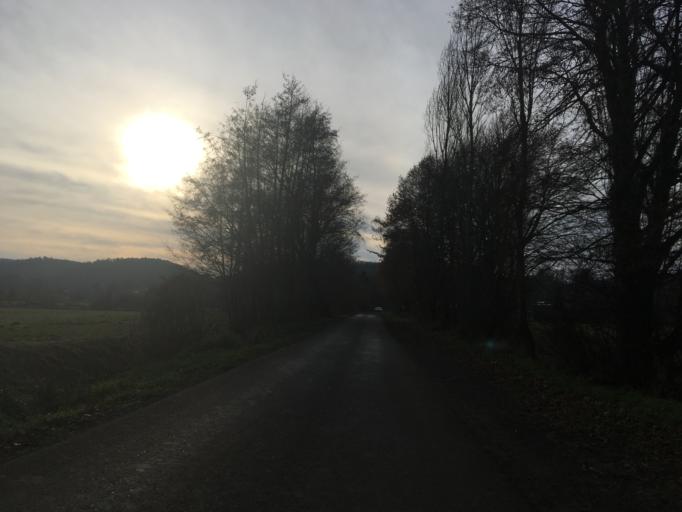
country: DE
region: Brandenburg
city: Falkenberg
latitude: 52.8092
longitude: 13.9641
